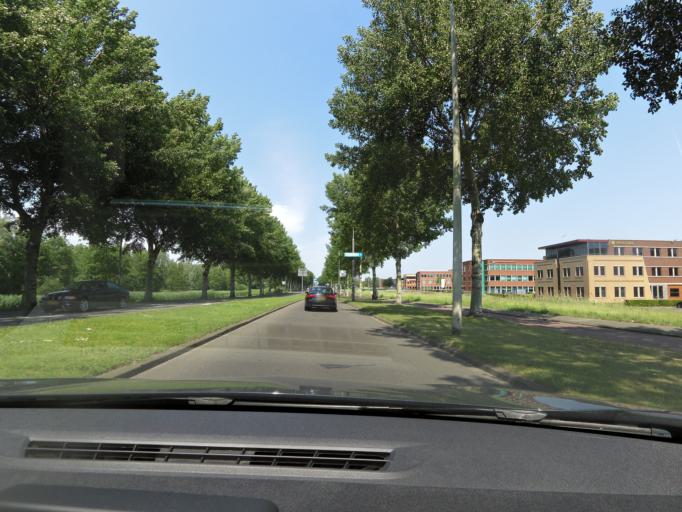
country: NL
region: South Holland
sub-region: Gemeente Rotterdam
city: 's-Gravenland
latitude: 51.9226
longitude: 4.5320
